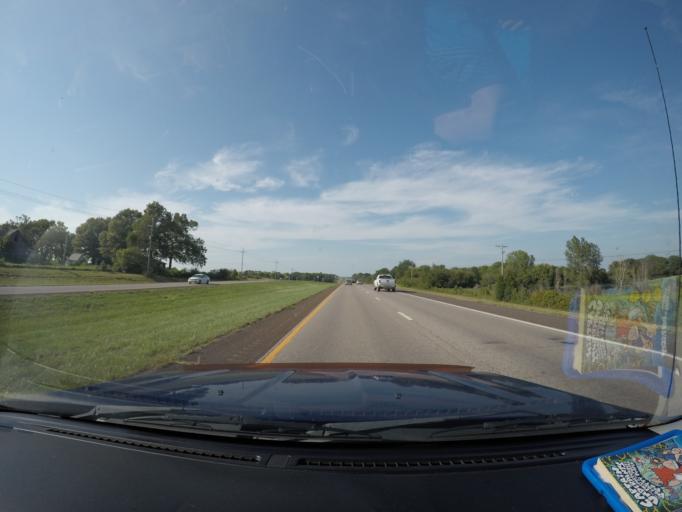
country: US
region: Kansas
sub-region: Leavenworth County
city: Lansing
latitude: 39.1929
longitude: -94.9003
